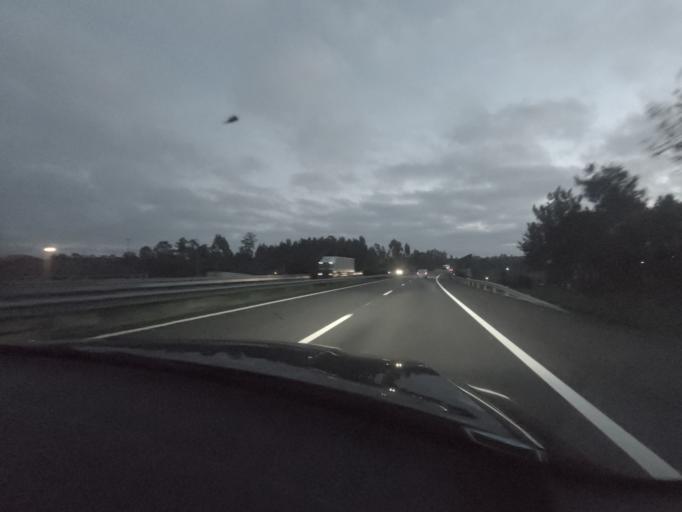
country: PT
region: Leiria
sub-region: Pombal
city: Pombal
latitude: 39.9126
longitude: -8.6848
